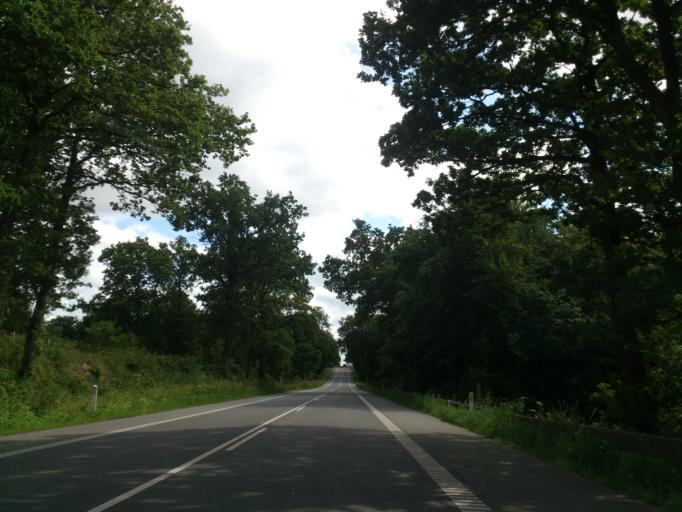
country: DK
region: South Denmark
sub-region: Aabenraa Kommune
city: Aabenraa
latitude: 54.9589
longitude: 9.4490
